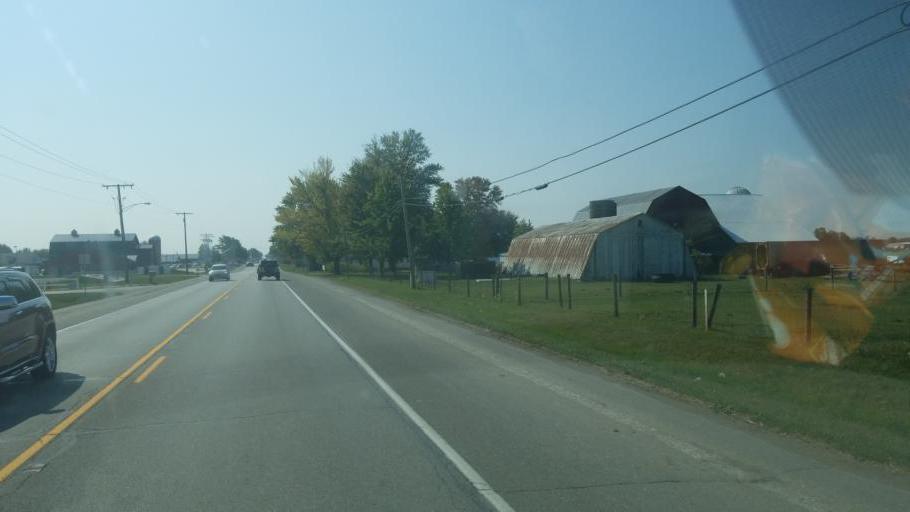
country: US
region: Indiana
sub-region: Elkhart County
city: Middlebury
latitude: 41.6616
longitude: -85.5804
